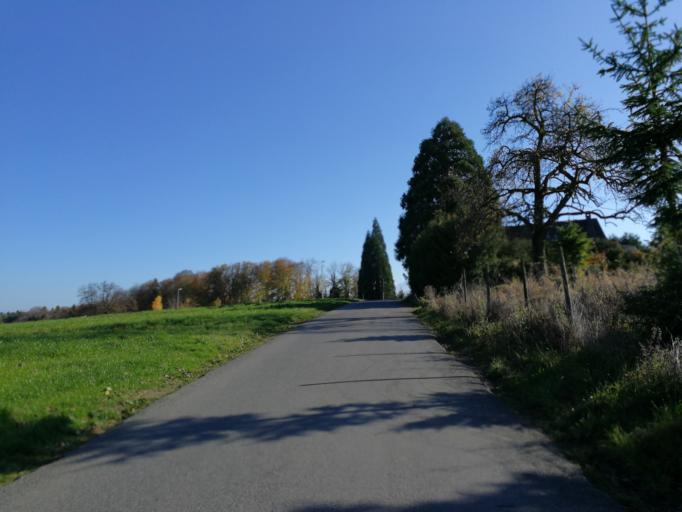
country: CH
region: Zurich
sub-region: Bezirk Uster
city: Egg
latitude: 47.2998
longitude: 8.6964
